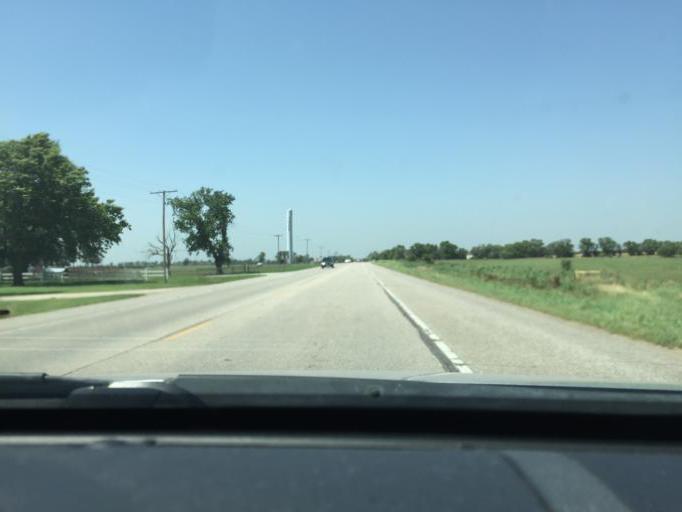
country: US
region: Kansas
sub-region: Reno County
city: Haven
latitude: 37.9501
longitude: -97.8668
